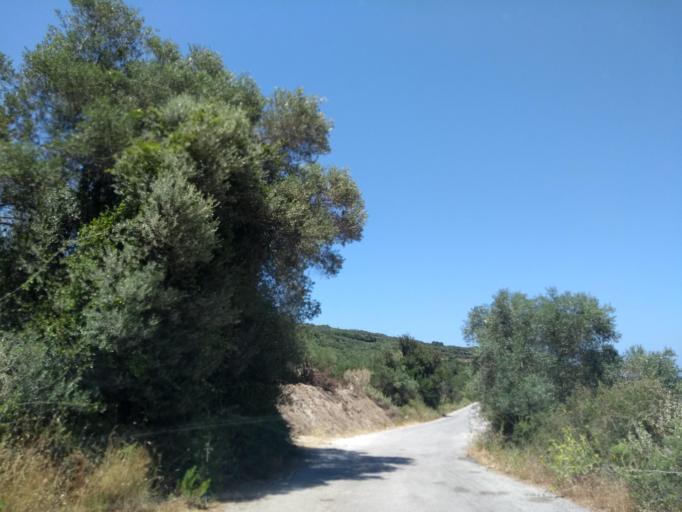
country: GR
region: Crete
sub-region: Nomos Chanias
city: Georgioupolis
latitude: 35.3233
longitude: 24.3139
